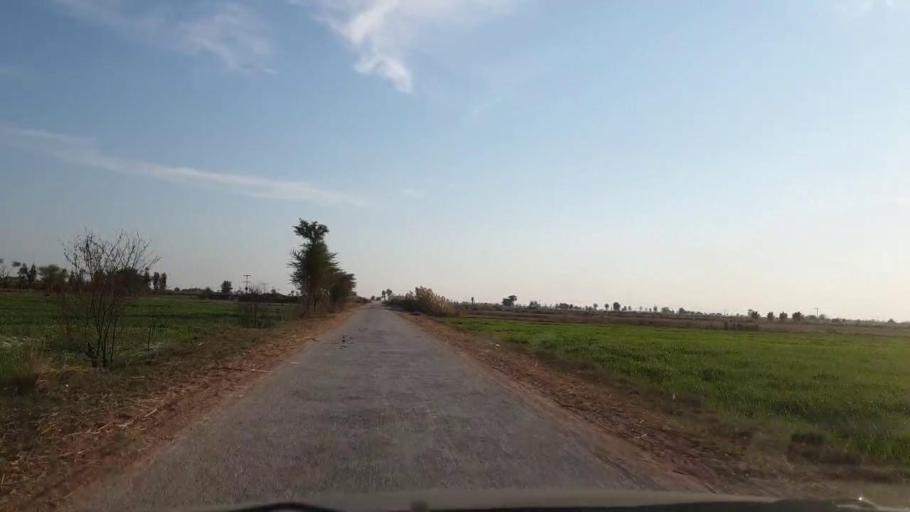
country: PK
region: Sindh
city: Khadro
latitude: 26.1825
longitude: 68.7501
